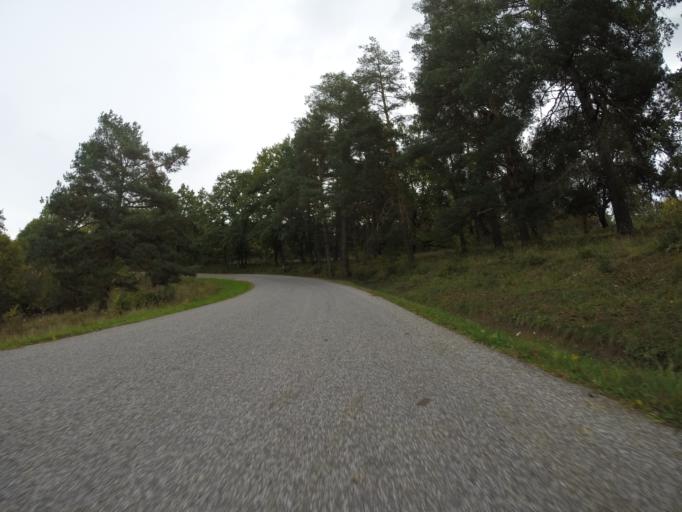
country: SK
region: Banskobystricky
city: Rimavska Sobota
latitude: 48.4977
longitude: 20.0958
